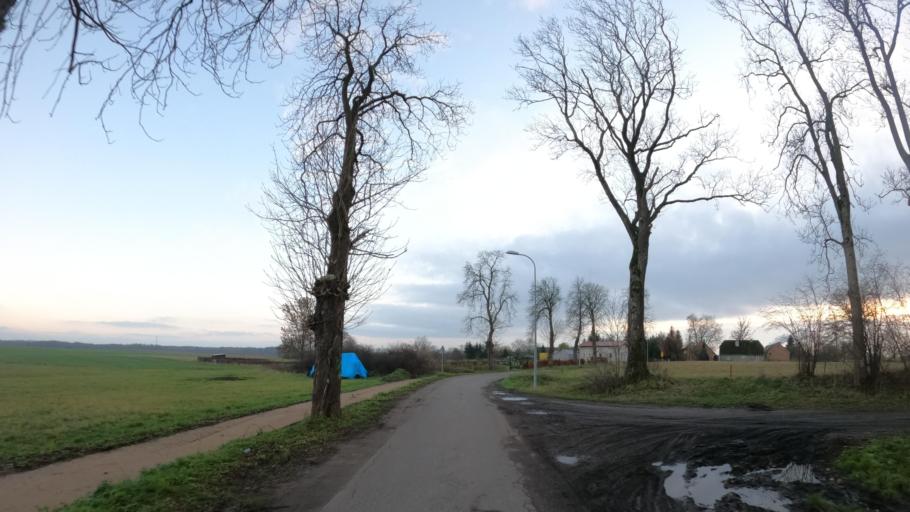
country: PL
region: West Pomeranian Voivodeship
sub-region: Powiat bialogardzki
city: Karlino
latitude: 54.0807
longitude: 15.8818
